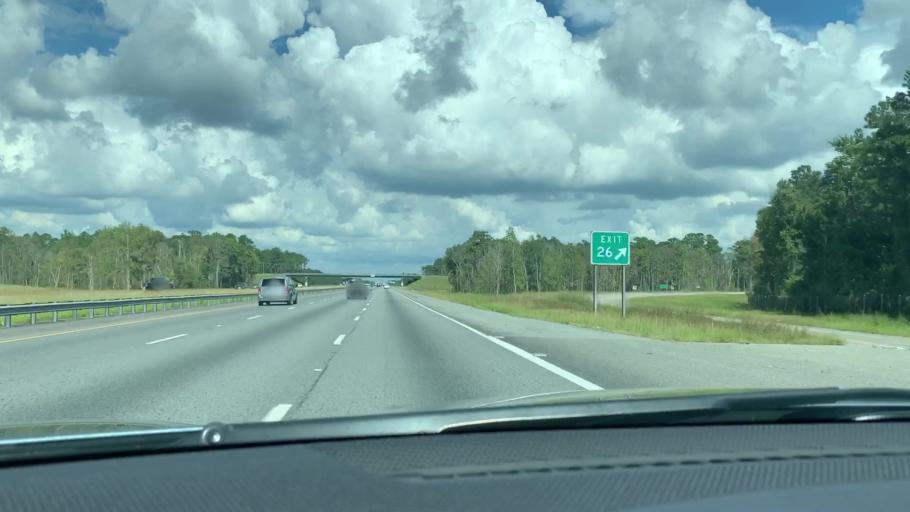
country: US
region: Georgia
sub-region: Glynn County
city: Brunswick
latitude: 31.0984
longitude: -81.5999
